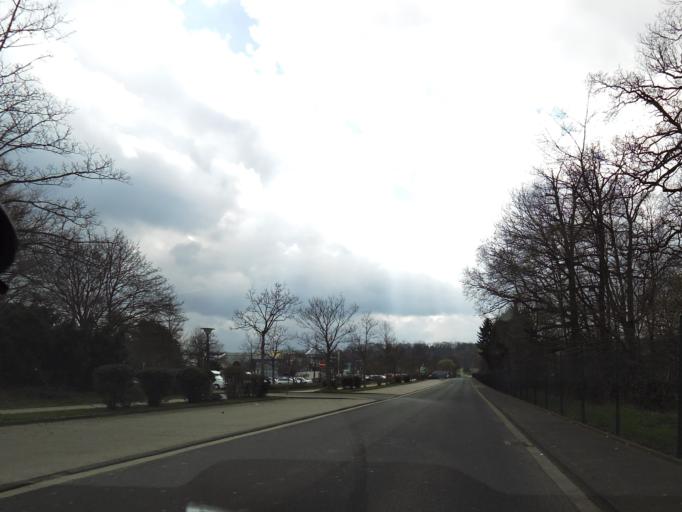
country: DE
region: North Rhine-Westphalia
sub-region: Regierungsbezirk Koln
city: Rheinbach
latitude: 50.6210
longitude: 6.9331
